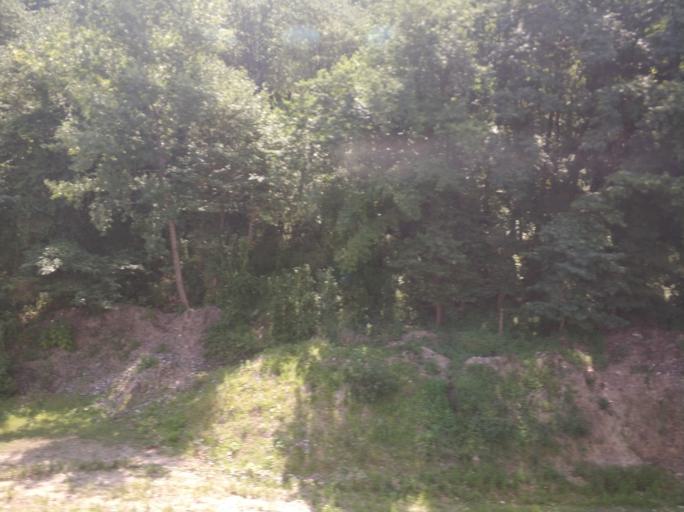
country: IR
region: Gilan
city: Pa'in-e Bazar-e Rudbar
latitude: 37.0042
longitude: 49.5892
